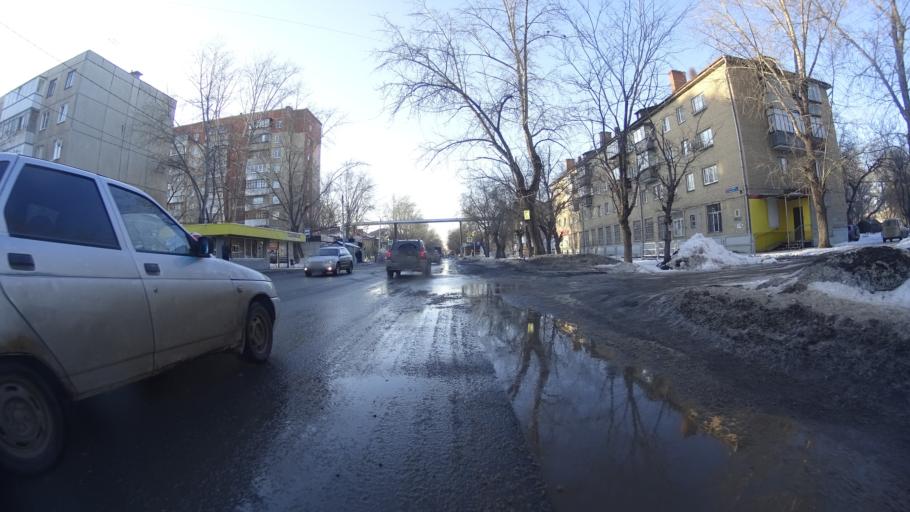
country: RU
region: Chelyabinsk
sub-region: Gorod Chelyabinsk
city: Chelyabinsk
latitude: 55.1268
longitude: 61.4719
